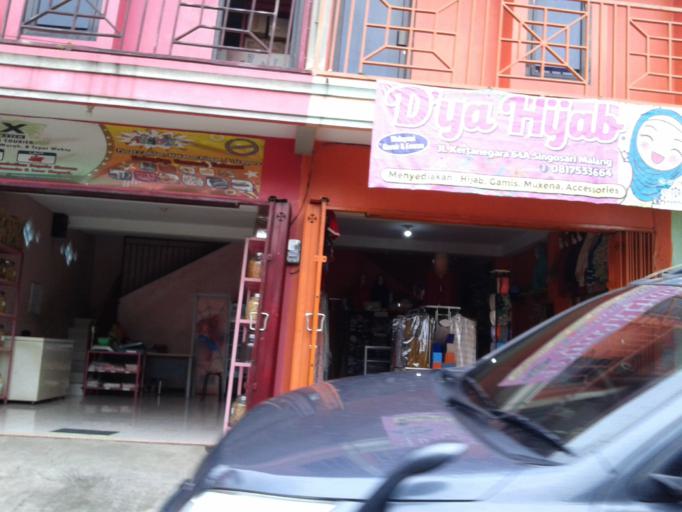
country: ID
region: East Java
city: Singosari
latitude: -7.8911
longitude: 112.6619
